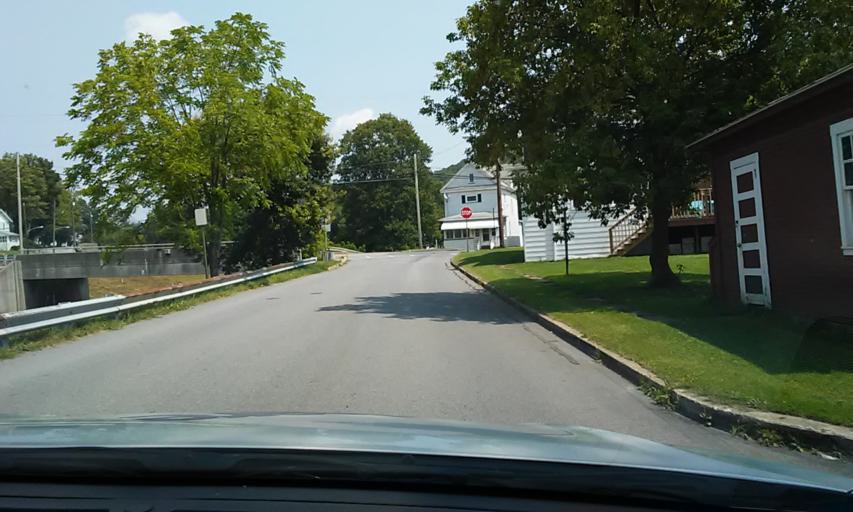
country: US
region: Pennsylvania
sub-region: Elk County
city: Ridgway
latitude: 41.4252
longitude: -78.7277
